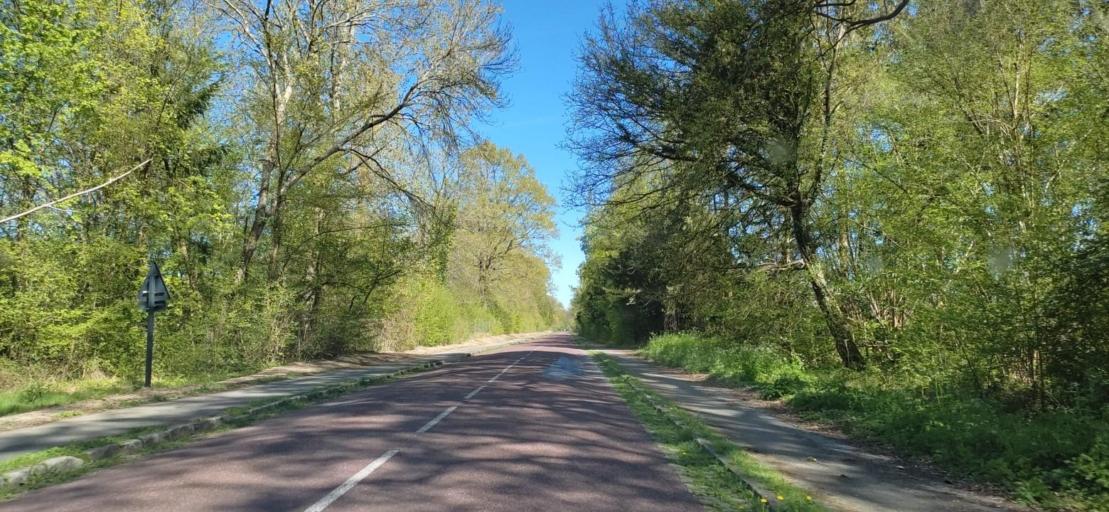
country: FR
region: Picardie
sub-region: Departement de l'Oise
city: Choisy-au-Bac
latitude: 49.4276
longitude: 2.8925
